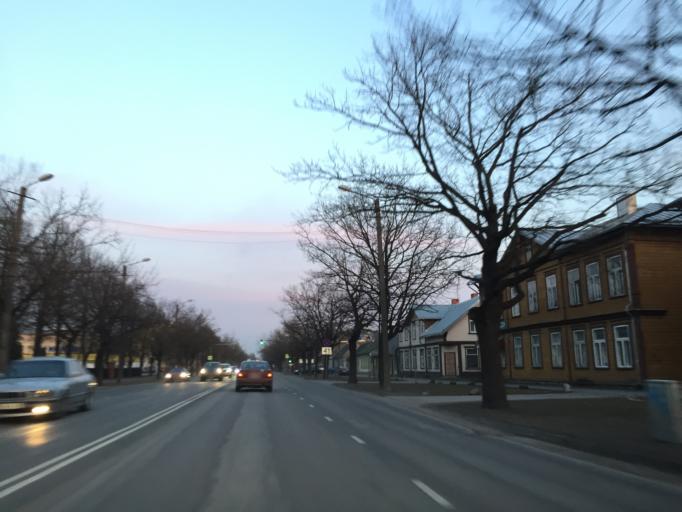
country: EE
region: Paernumaa
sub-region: Paernu linn
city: Parnu
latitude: 58.3805
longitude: 24.5245
